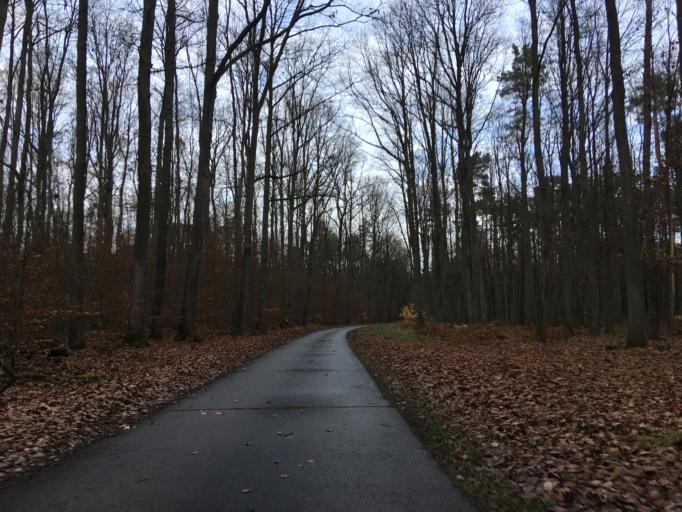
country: DE
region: Brandenburg
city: Tauer
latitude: 51.9463
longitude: 14.5167
